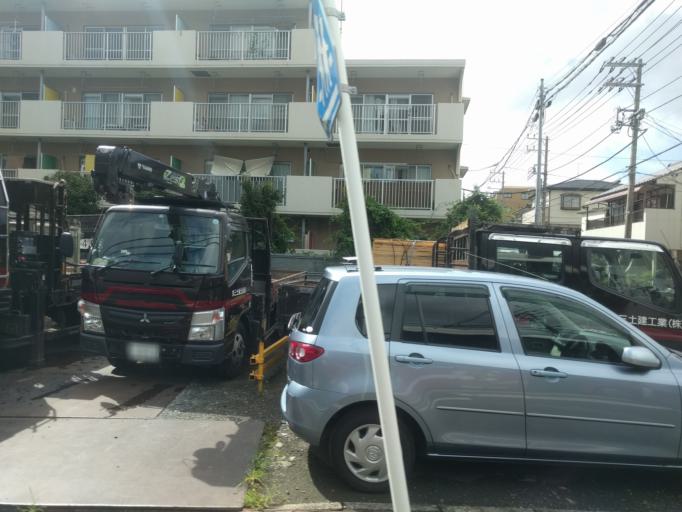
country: JP
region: Saitama
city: Shimotoda
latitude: 35.8310
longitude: 139.6769
